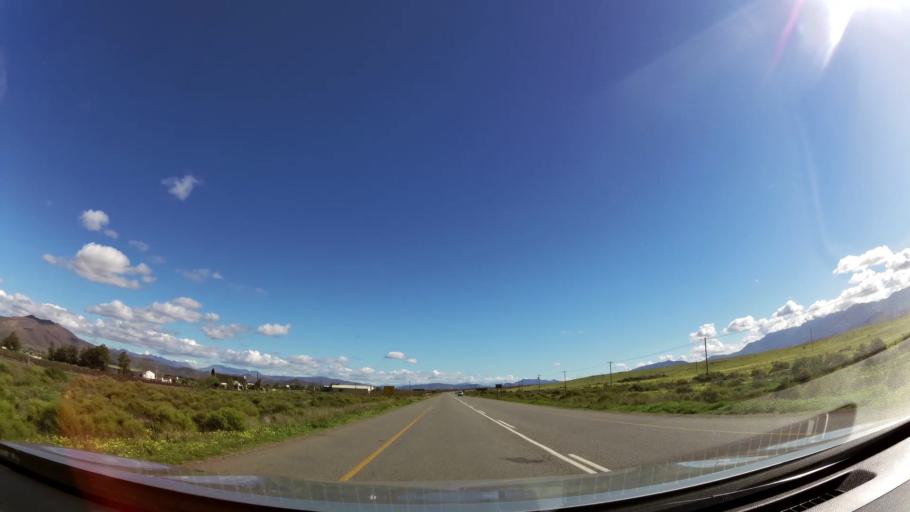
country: ZA
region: Western Cape
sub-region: Cape Winelands District Municipality
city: Ashton
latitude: -33.8394
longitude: 20.0173
